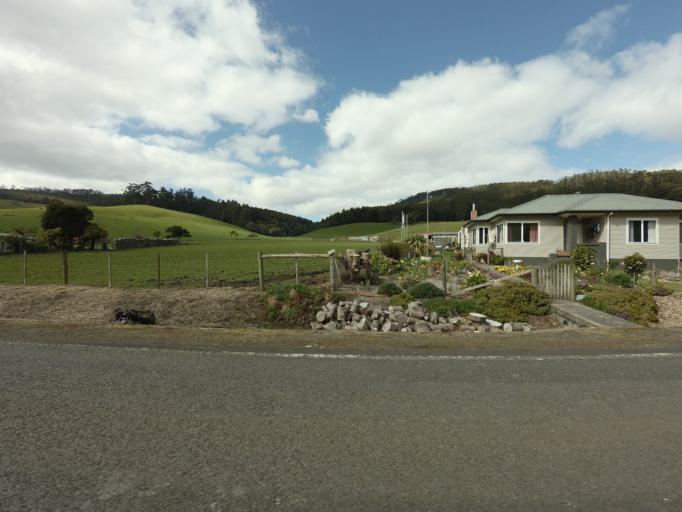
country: AU
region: Tasmania
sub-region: Huon Valley
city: Cygnet
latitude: -43.2917
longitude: 147.0110
